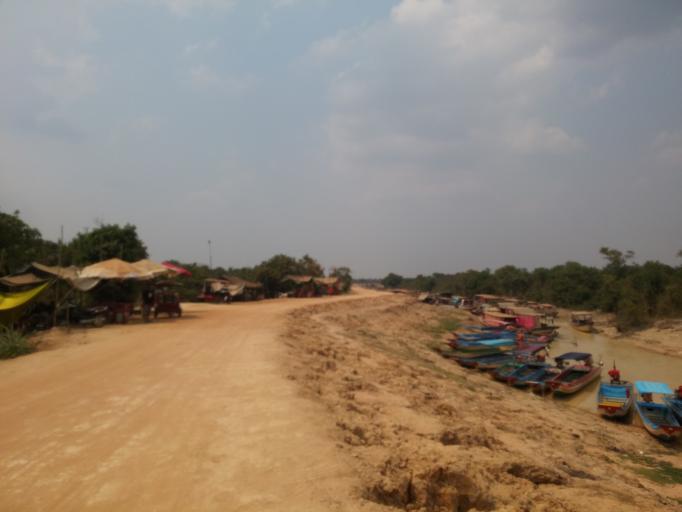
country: KH
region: Siem Reap
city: Siem Reap
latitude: 13.2261
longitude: 103.9746
